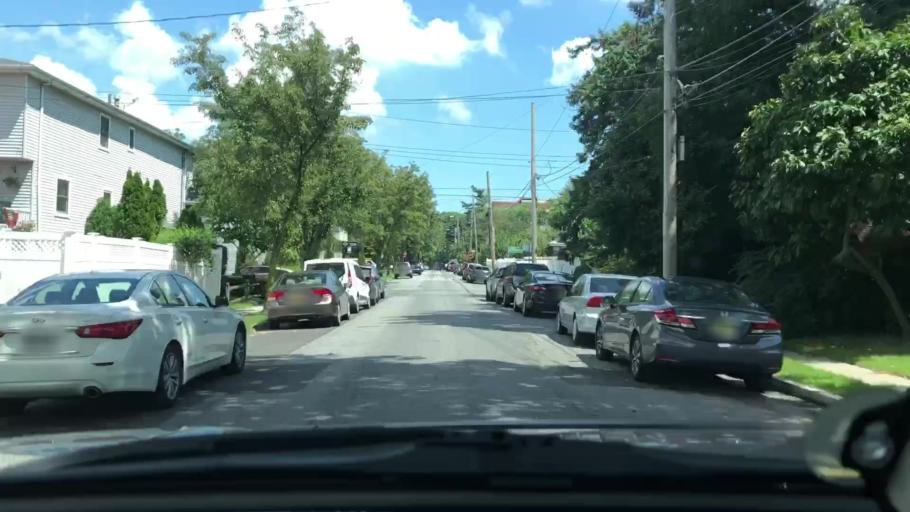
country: US
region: New Jersey
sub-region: Hudson County
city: Bayonne
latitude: 40.6286
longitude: -74.1104
